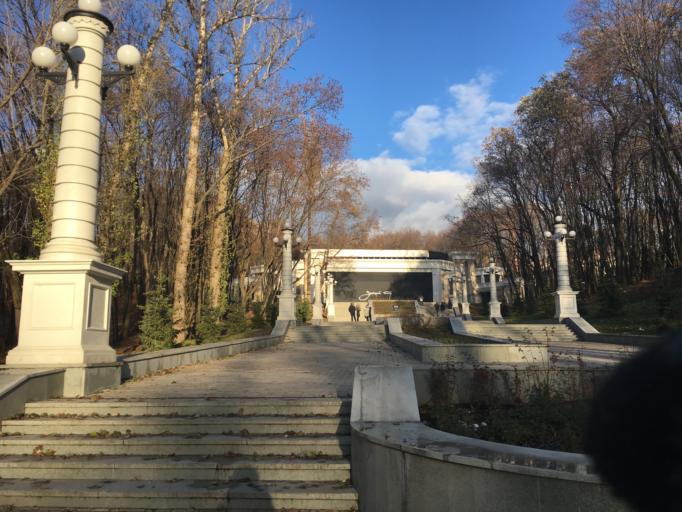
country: RU
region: Voronezj
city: Voronezh
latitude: 51.6990
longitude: 39.2192
